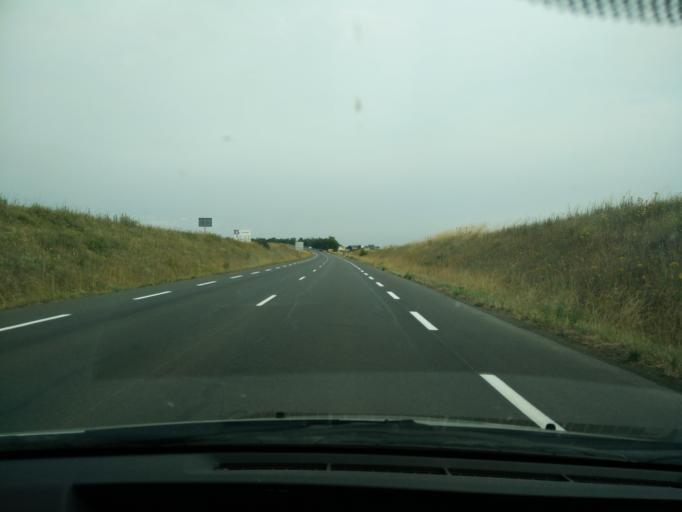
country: FR
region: Poitou-Charentes
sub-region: Departement des Deux-Sevres
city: Louzy
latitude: 47.0044
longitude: -0.1943
